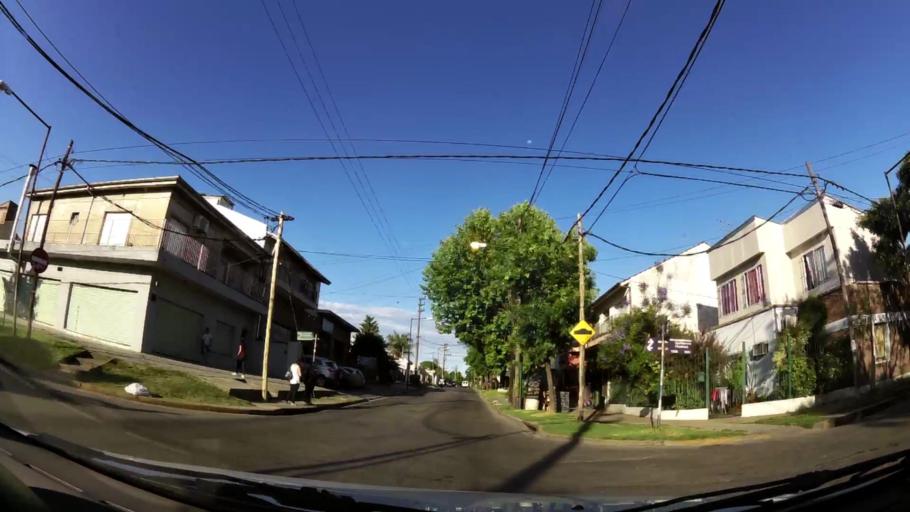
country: AR
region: Buenos Aires
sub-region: Partido de San Isidro
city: San Isidro
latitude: -34.4722
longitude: -58.5503
